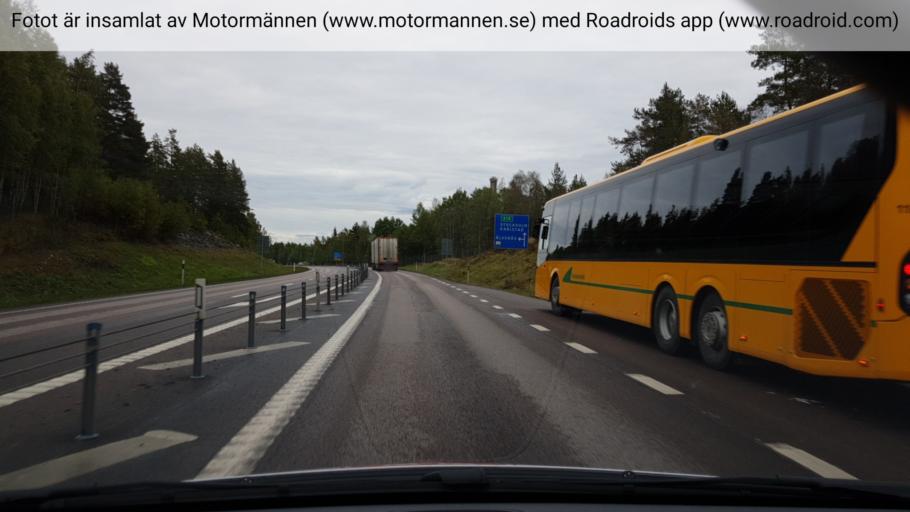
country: SE
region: Vaermland
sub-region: Karlstads Kommun
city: Valberg
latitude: 59.3711
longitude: 13.1677
